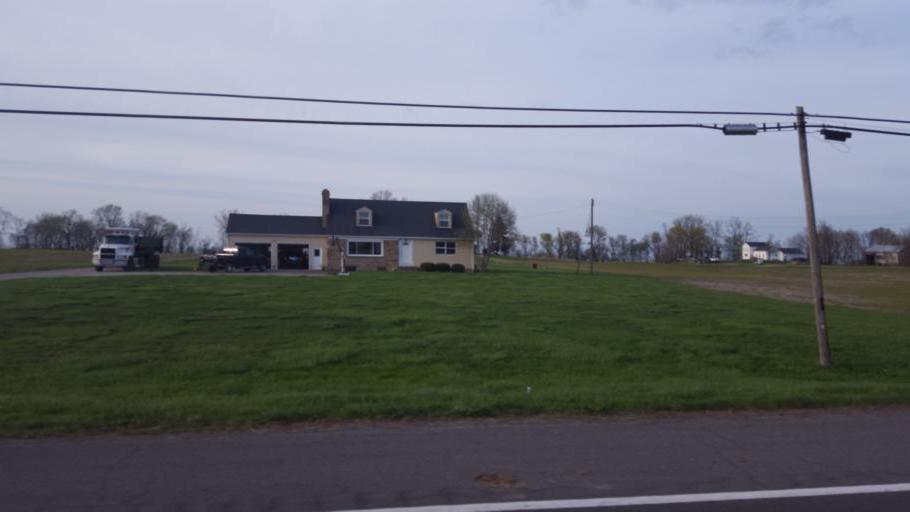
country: US
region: Ohio
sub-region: Erie County
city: Huron
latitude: 41.3784
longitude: -82.4938
